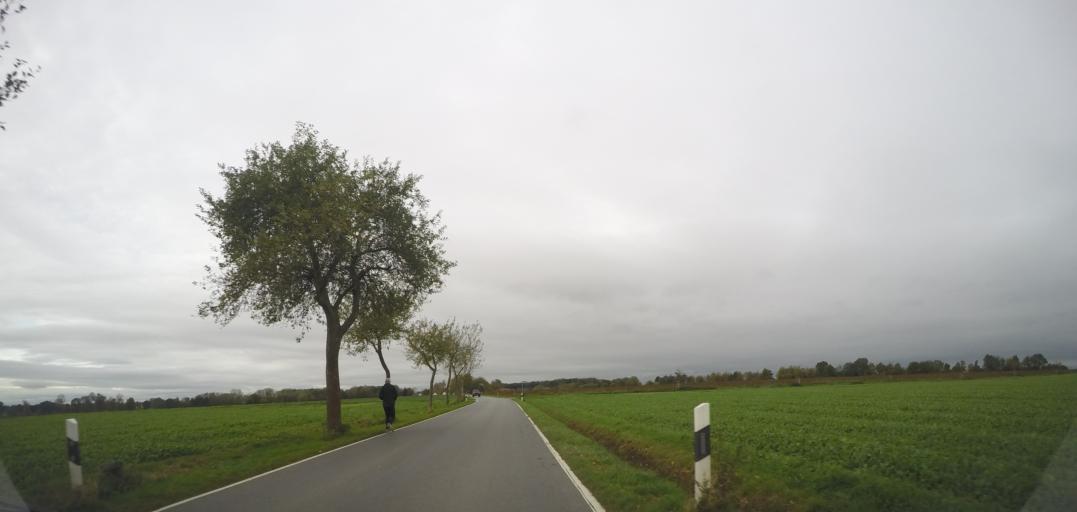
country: DE
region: North Rhine-Westphalia
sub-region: Regierungsbezirk Arnsberg
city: Bad Sassendorf
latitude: 51.6354
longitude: 8.2130
